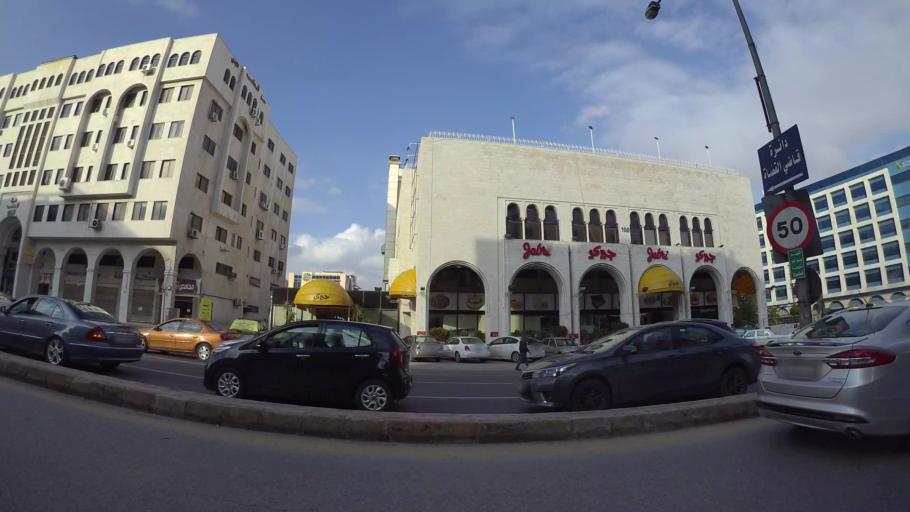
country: JO
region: Amman
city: Al Jubayhah
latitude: 31.9871
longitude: 35.8770
